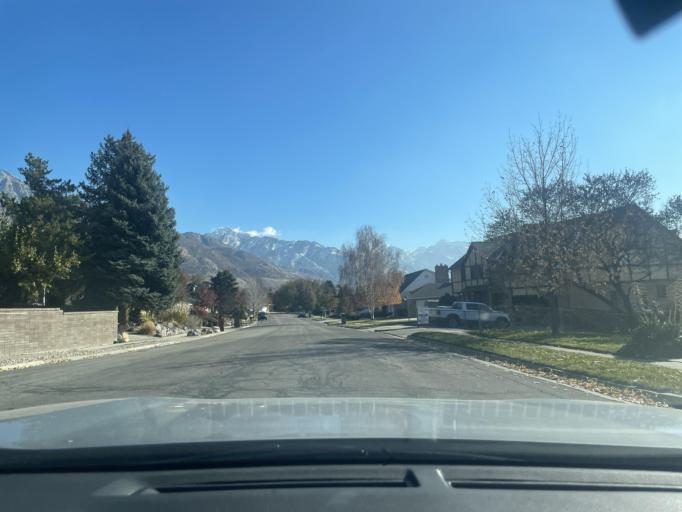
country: US
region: Utah
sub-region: Salt Lake County
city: Holladay
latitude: 40.6773
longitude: -111.8295
